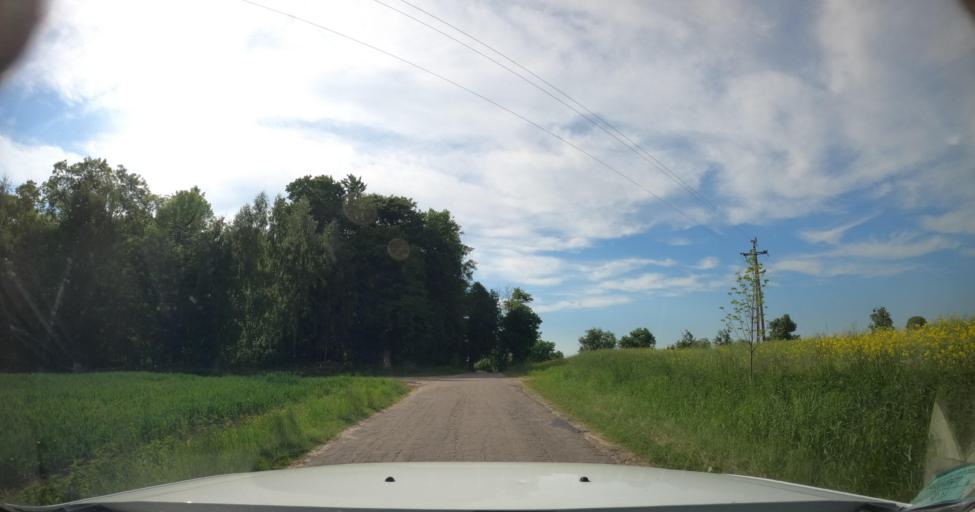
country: PL
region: Warmian-Masurian Voivodeship
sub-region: Powiat ostrodzki
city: Morag
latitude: 54.0193
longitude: 19.9164
